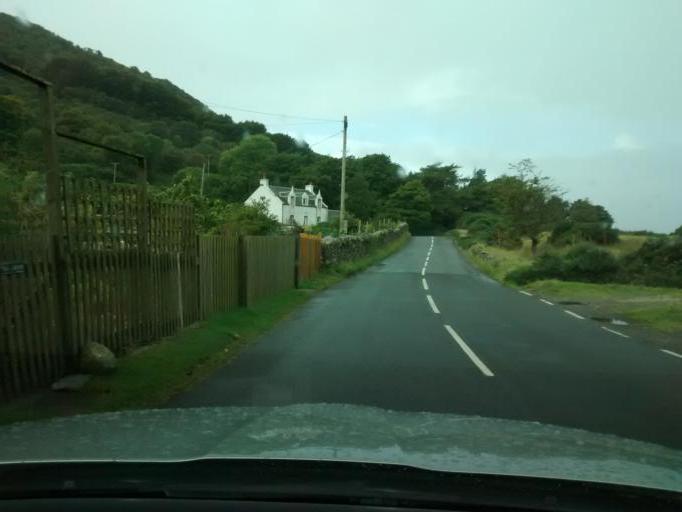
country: GB
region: Scotland
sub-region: North Ayrshire
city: Isle of Arran
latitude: 55.7017
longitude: -5.2848
